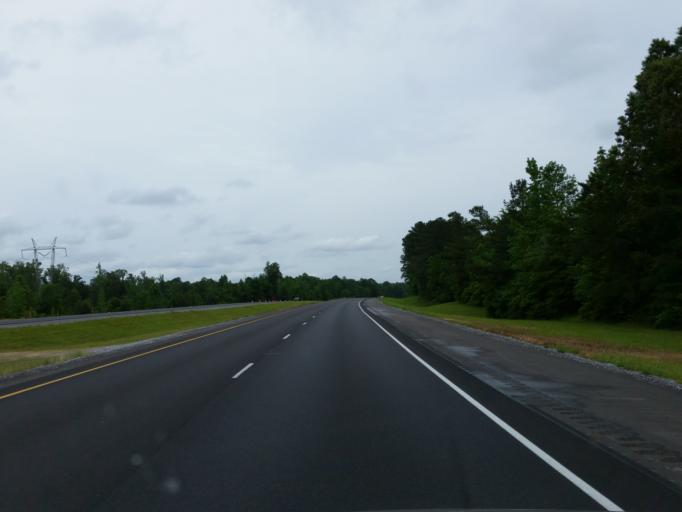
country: US
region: Mississippi
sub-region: Jones County
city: Sharon
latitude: 31.9215
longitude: -89.0040
